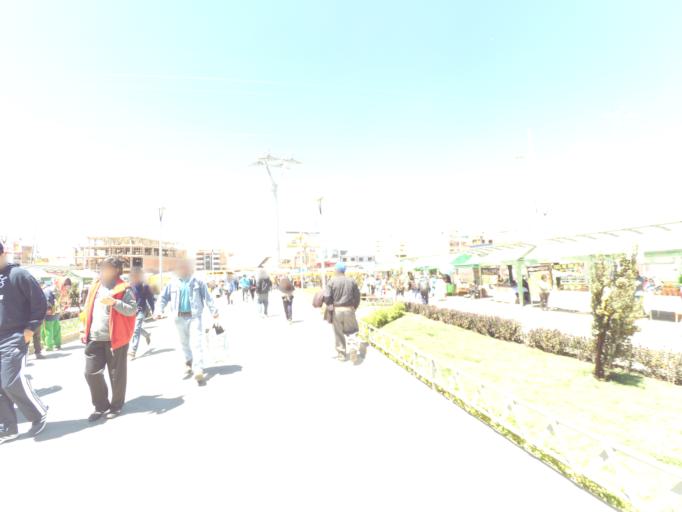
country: BO
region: La Paz
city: La Paz
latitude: -16.4976
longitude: -68.1649
